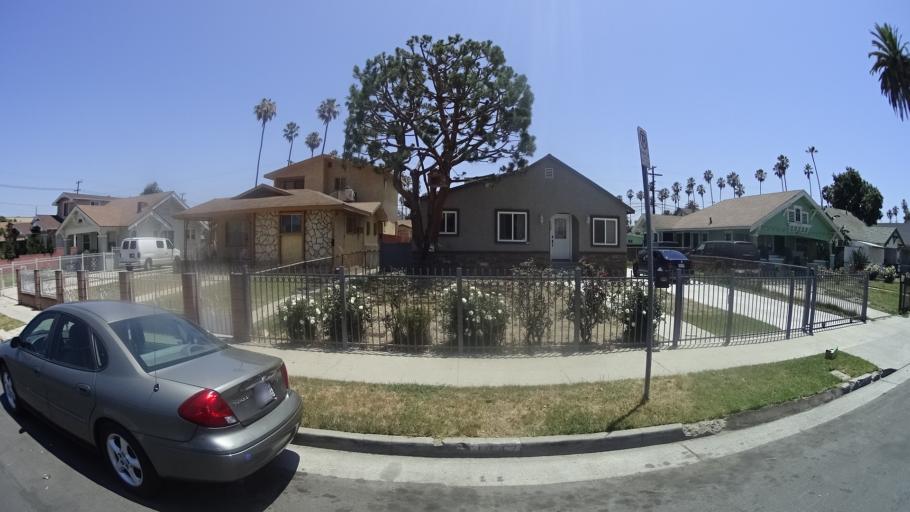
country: US
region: California
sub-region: Los Angeles County
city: View Park-Windsor Hills
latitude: 33.9970
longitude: -118.3105
